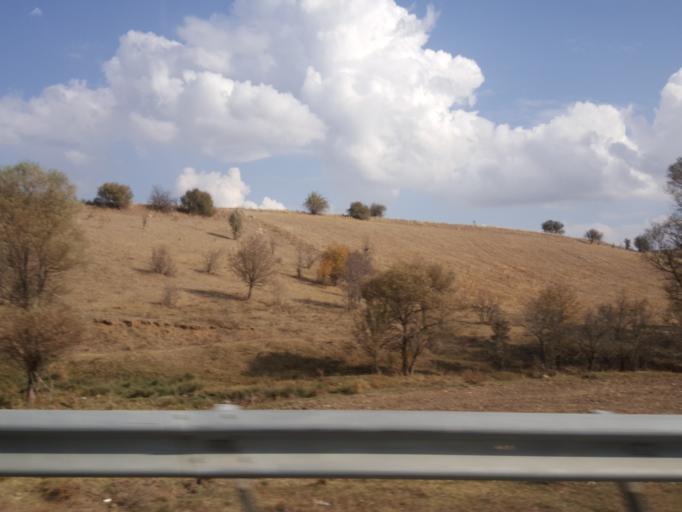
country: TR
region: Corum
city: Alaca
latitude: 40.3013
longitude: 34.6547
